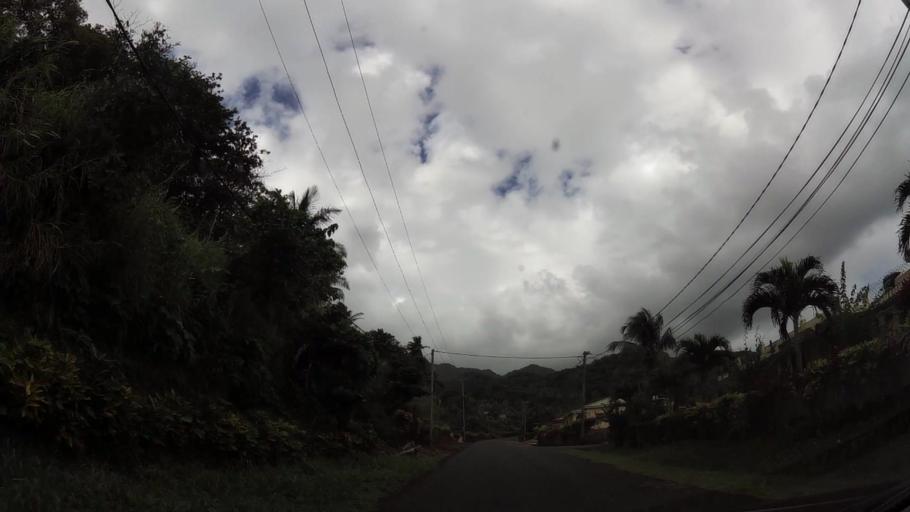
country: DM
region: Saint David
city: Castle Bruce
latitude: 15.4353
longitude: -61.2594
